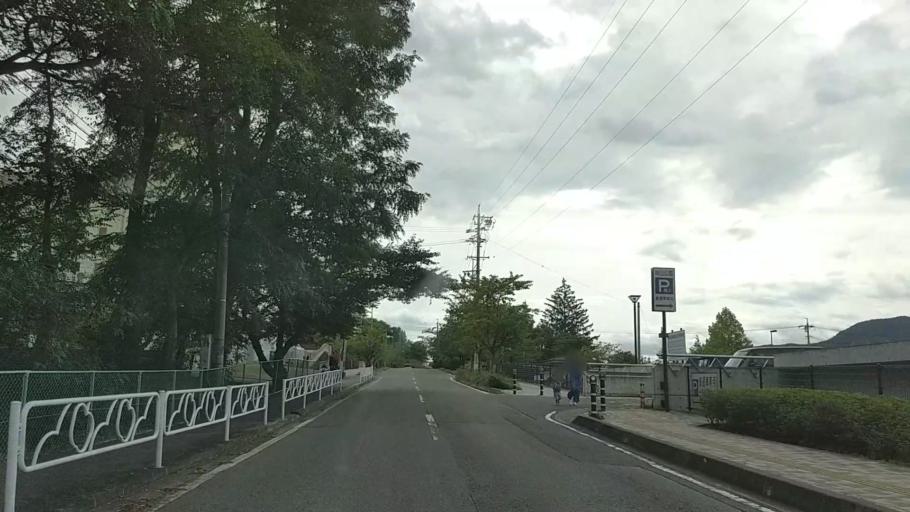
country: JP
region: Nagano
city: Nagano-shi
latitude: 36.6645
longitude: 138.1932
